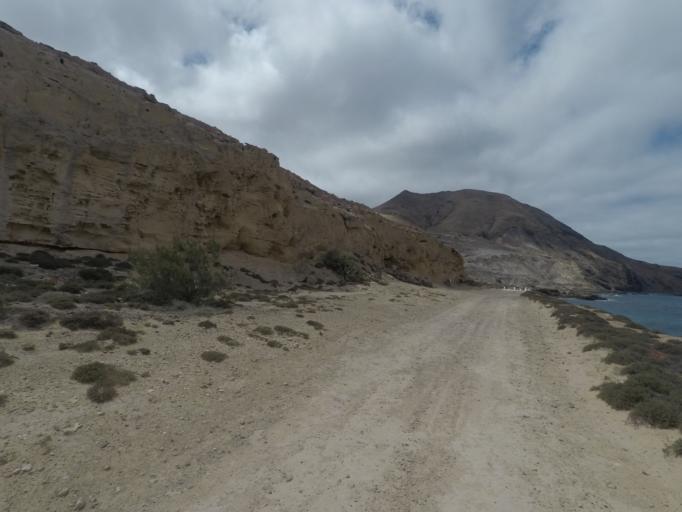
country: PT
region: Madeira
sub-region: Porto Santo
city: Vila de Porto Santo
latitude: 33.0672
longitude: -16.2970
